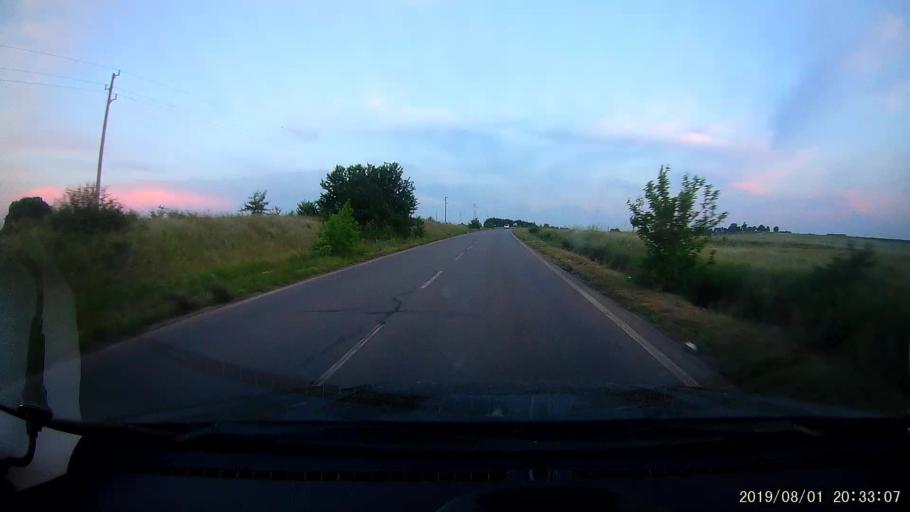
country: BG
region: Yambol
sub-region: Obshtina Elkhovo
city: Elkhovo
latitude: 42.1108
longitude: 26.5319
